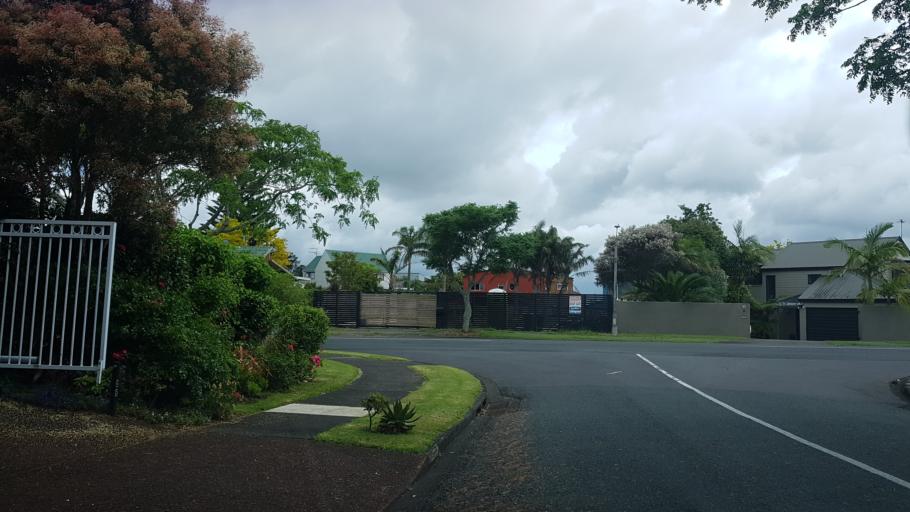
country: NZ
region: Auckland
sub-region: Auckland
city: Rosebank
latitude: -36.8321
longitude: 174.6589
